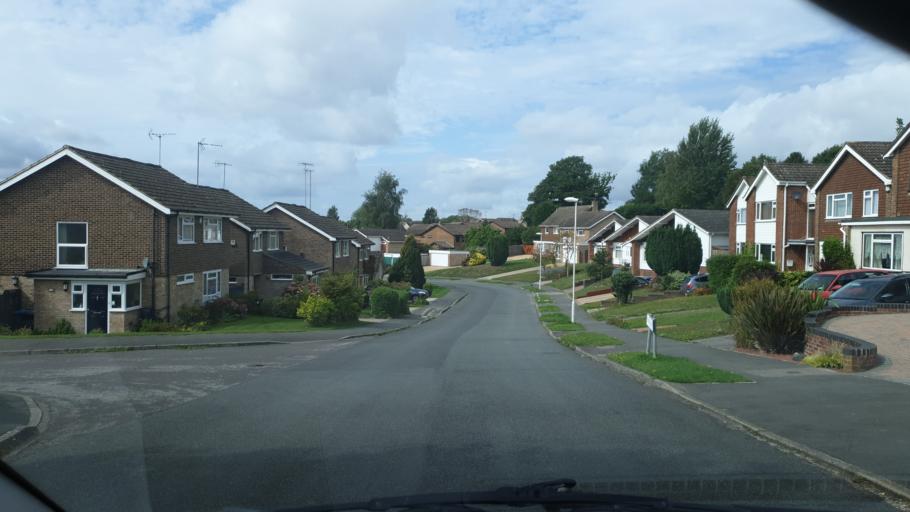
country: GB
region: England
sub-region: West Sussex
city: East Grinstead
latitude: 51.1365
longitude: 0.0078
